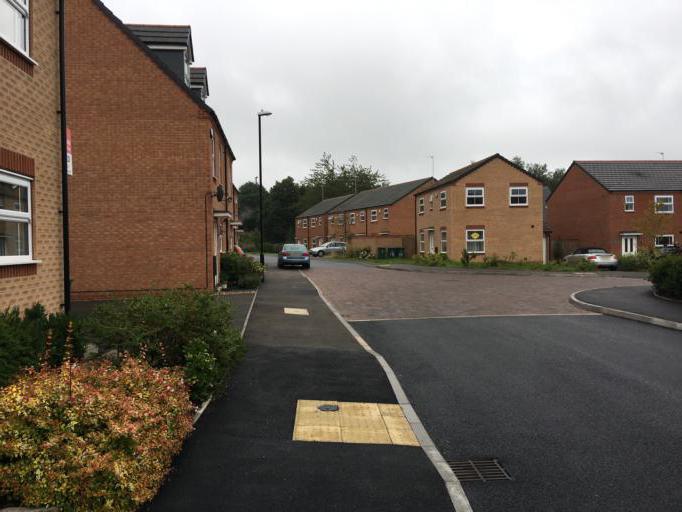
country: GB
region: England
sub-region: Coventry
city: Coventry
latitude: 52.3960
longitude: -1.5575
